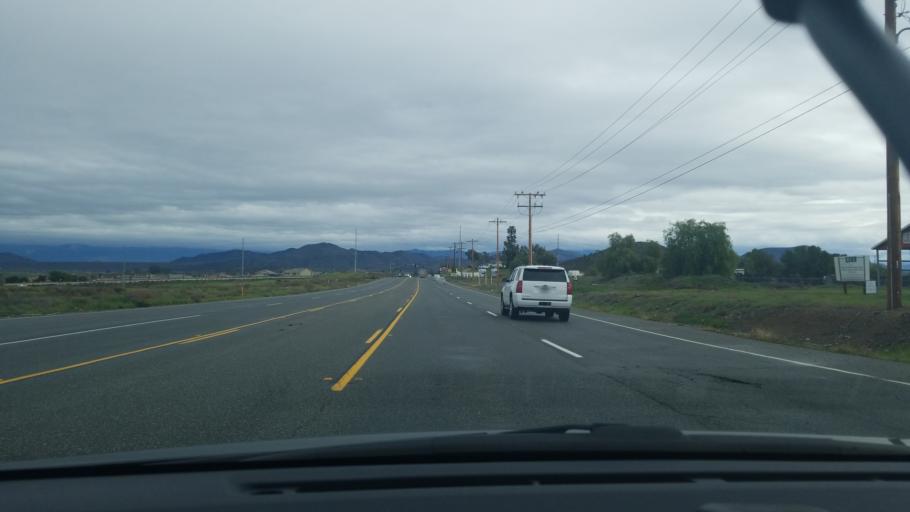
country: US
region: California
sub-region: Riverside County
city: Murrieta Hot Springs
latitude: 33.6415
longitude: -117.1411
